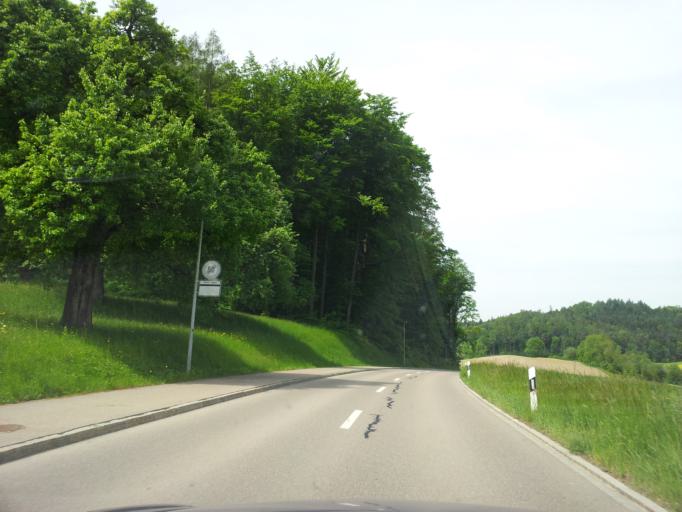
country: CH
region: Zurich
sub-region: Bezirk Dielsdorf
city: Otelfingen
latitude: 47.4691
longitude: 8.3972
